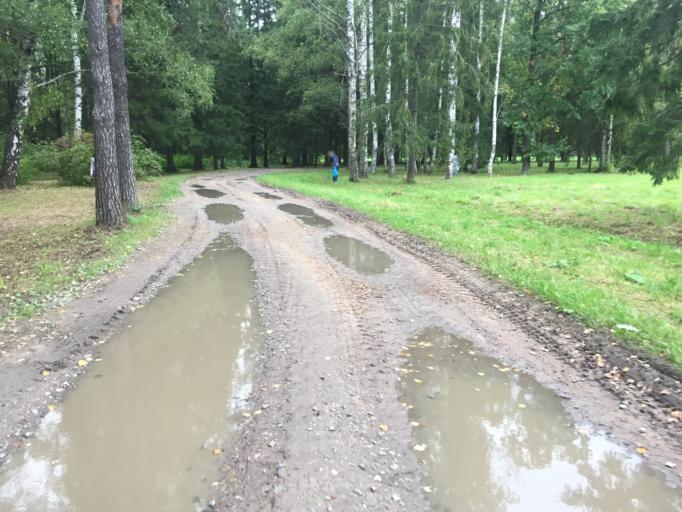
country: RU
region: St.-Petersburg
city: Pushkin
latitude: 59.7171
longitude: 30.3814
